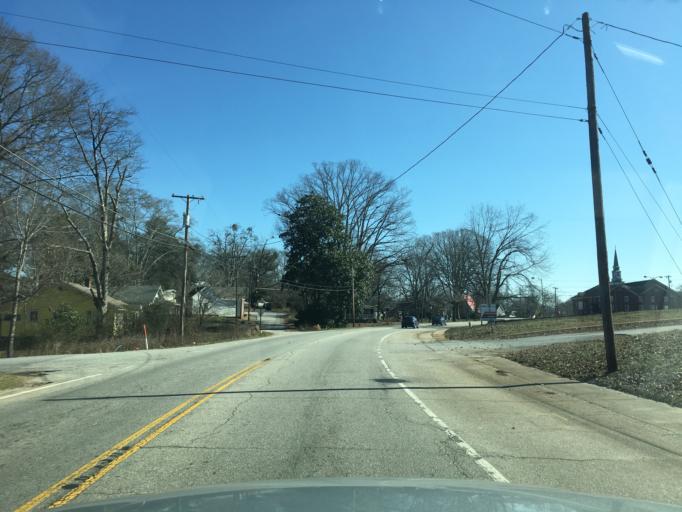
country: US
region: South Carolina
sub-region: Pickens County
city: Liberty
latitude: 34.7857
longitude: -82.6885
